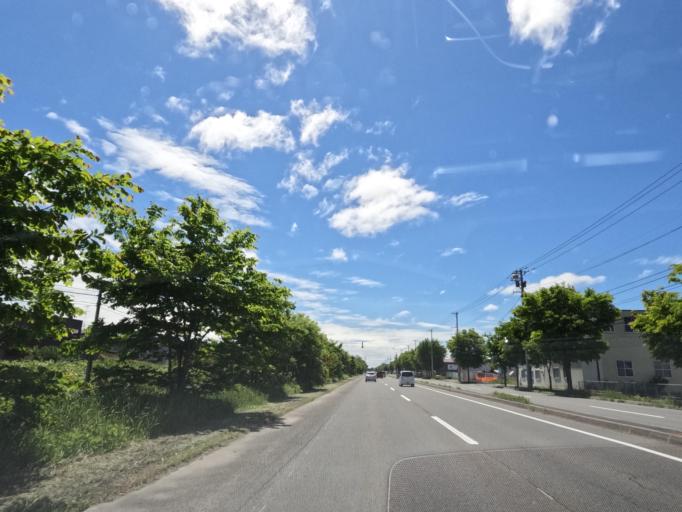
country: JP
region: Hokkaido
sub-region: Asahikawa-shi
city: Asahikawa
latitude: 43.7383
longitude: 142.3613
